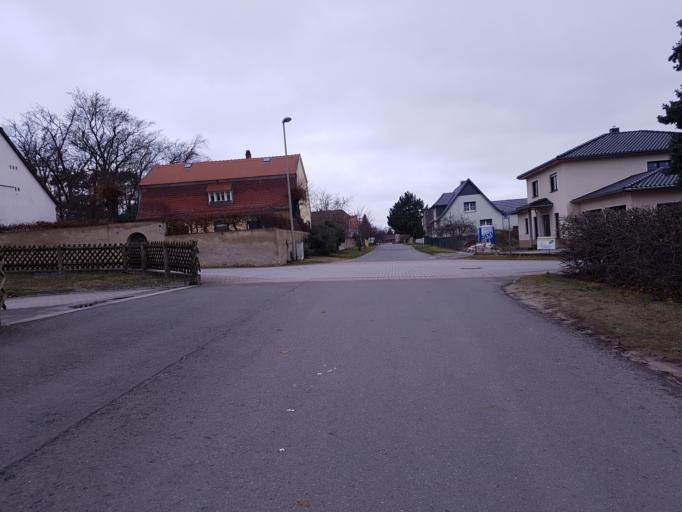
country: DE
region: Brandenburg
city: Groden
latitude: 51.4045
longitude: 13.5691
